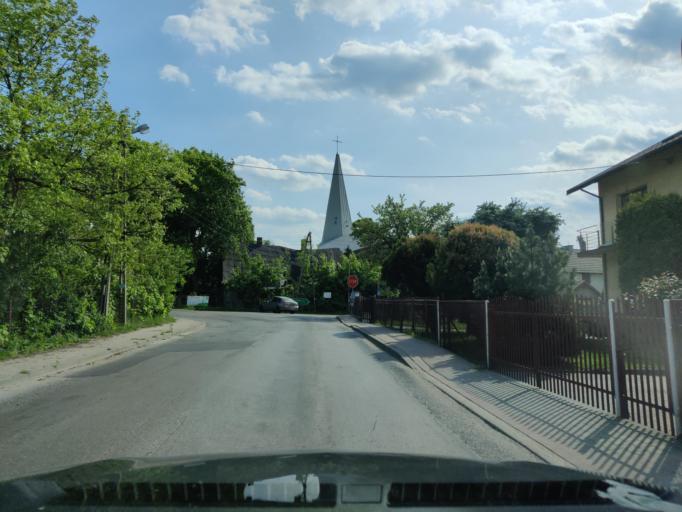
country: PL
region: Silesian Voivodeship
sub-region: Dabrowa Gornicza
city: Dabrowa Gornicza
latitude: 50.3915
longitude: 19.2411
